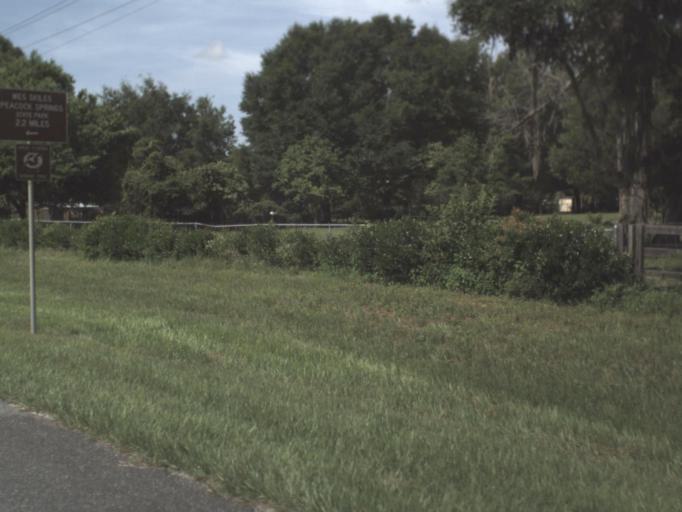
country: US
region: Florida
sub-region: Lafayette County
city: Mayo
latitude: 30.1230
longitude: -83.1696
